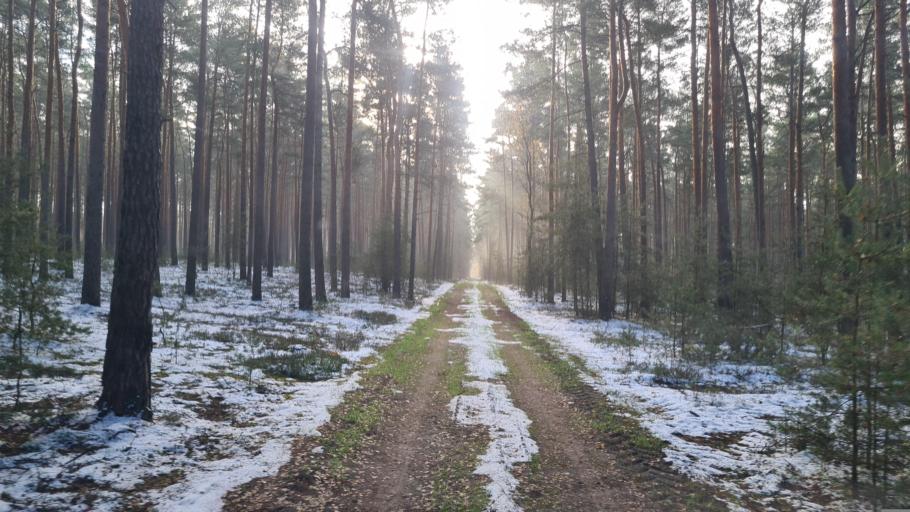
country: DE
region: Brandenburg
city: Bronkow
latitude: 51.6663
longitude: 13.8955
